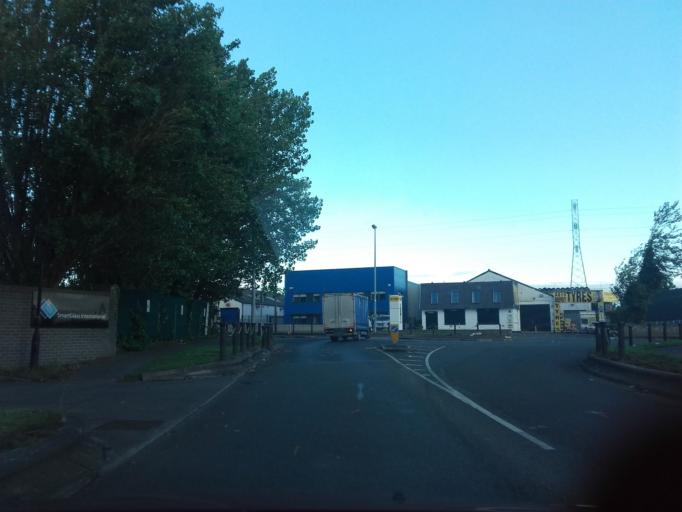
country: IE
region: Leinster
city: Tallaght
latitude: 53.2965
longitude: -6.3758
